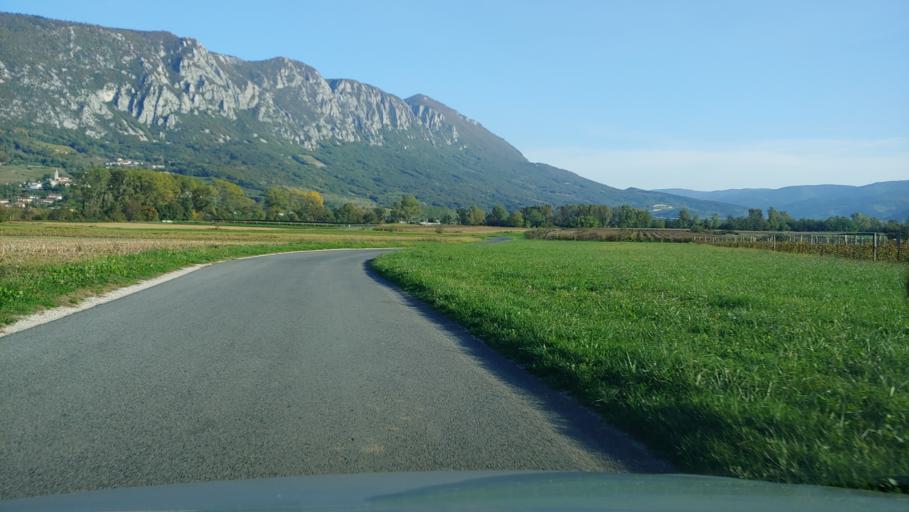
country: SI
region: Vipava
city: Vipava
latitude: 45.8393
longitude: 13.9430
